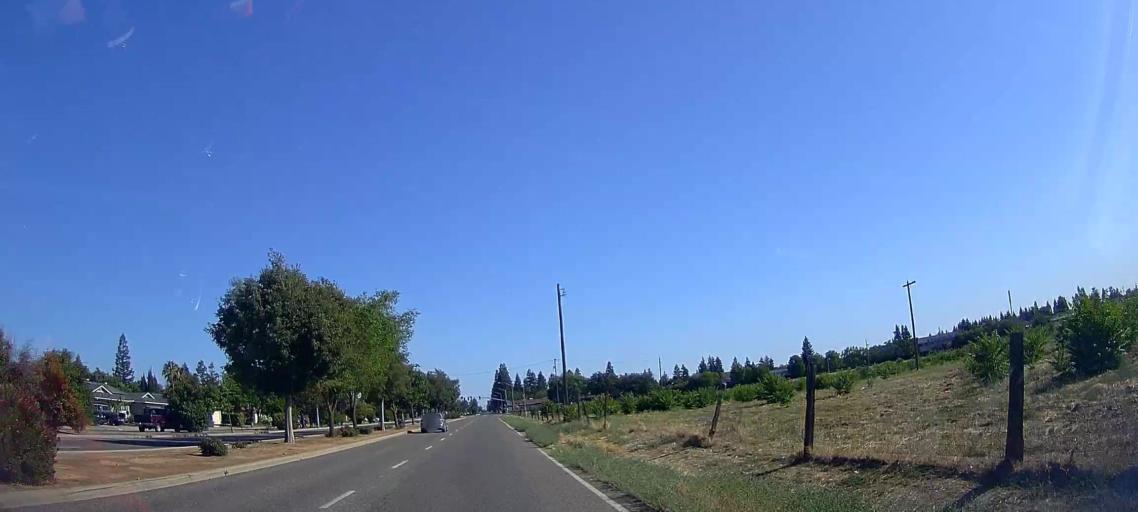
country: US
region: California
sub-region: Fresno County
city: Clovis
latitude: 36.8326
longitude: -119.7814
